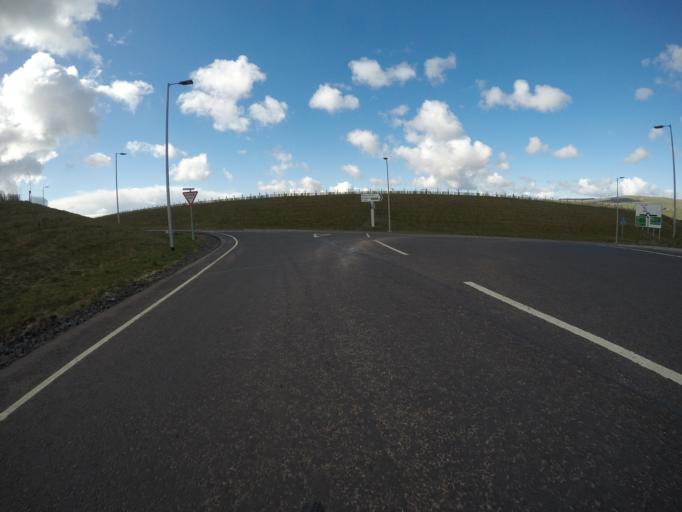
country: GB
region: Scotland
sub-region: North Ayrshire
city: Dalry
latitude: 55.7128
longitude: -4.6924
